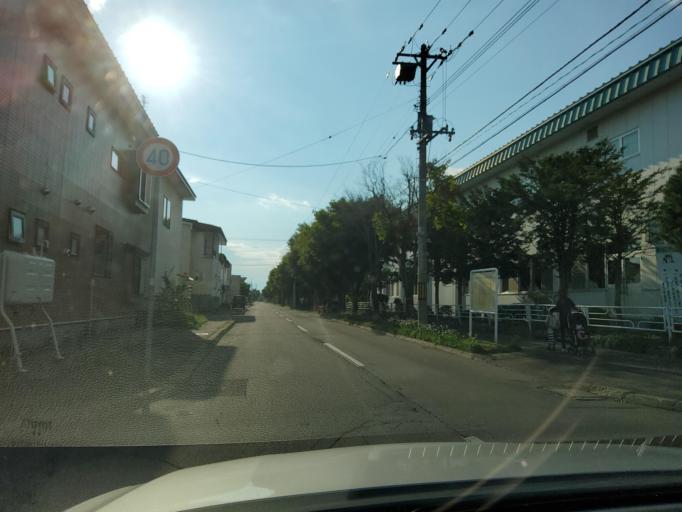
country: JP
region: Hokkaido
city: Obihiro
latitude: 42.9120
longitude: 143.1698
